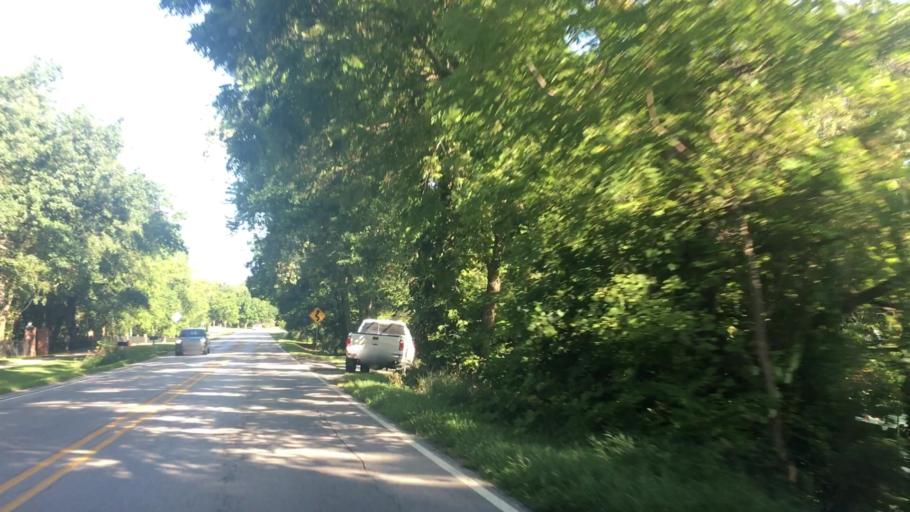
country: US
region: Iowa
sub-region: Johnson County
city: Coralville
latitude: 41.7053
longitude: -91.5472
